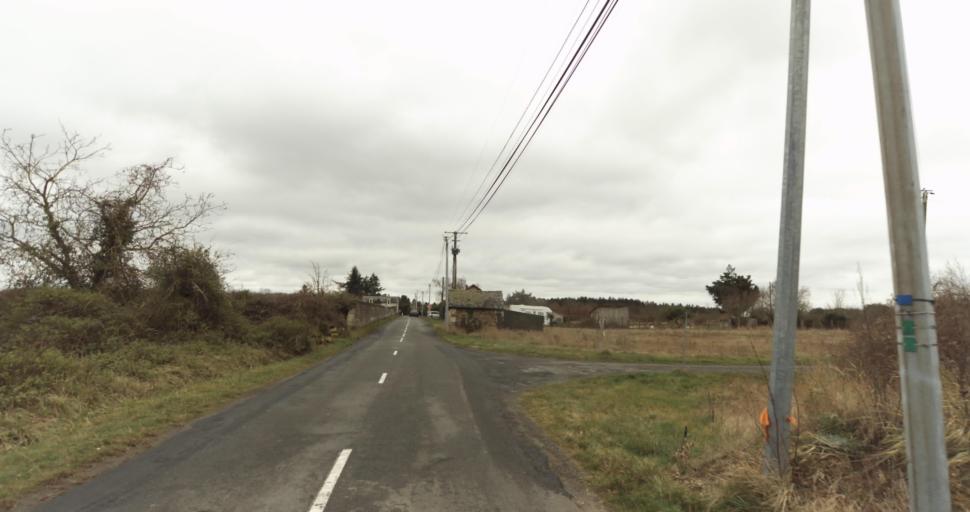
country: FR
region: Pays de la Loire
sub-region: Departement de Maine-et-Loire
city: Distre
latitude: 47.2432
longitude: -0.1062
